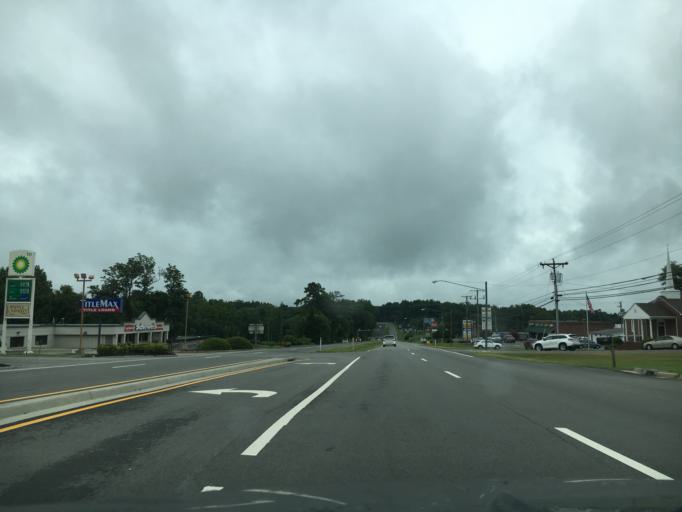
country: US
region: Virginia
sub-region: Halifax County
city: Halifax
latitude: 36.7342
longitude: -78.9182
